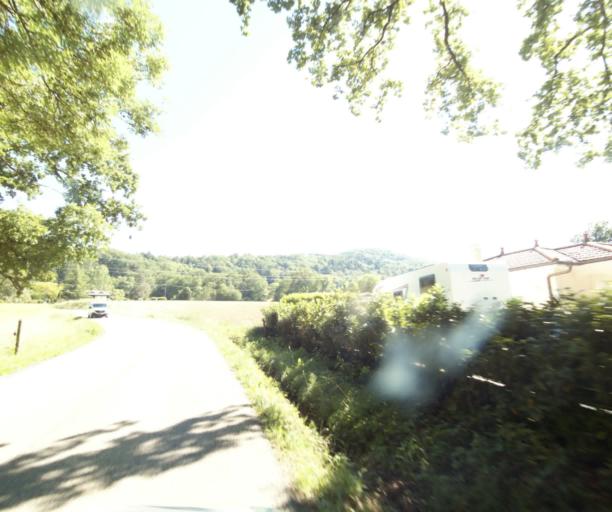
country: FR
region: Rhone-Alpes
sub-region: Departement de la Haute-Savoie
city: Sciez
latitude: 46.3241
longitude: 6.3814
